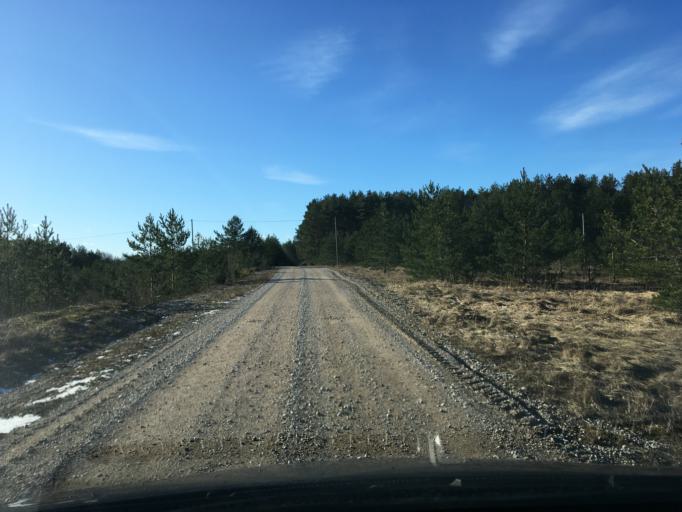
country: EE
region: Laeaene
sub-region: Lihula vald
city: Lihula
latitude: 58.5814
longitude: 23.7041
